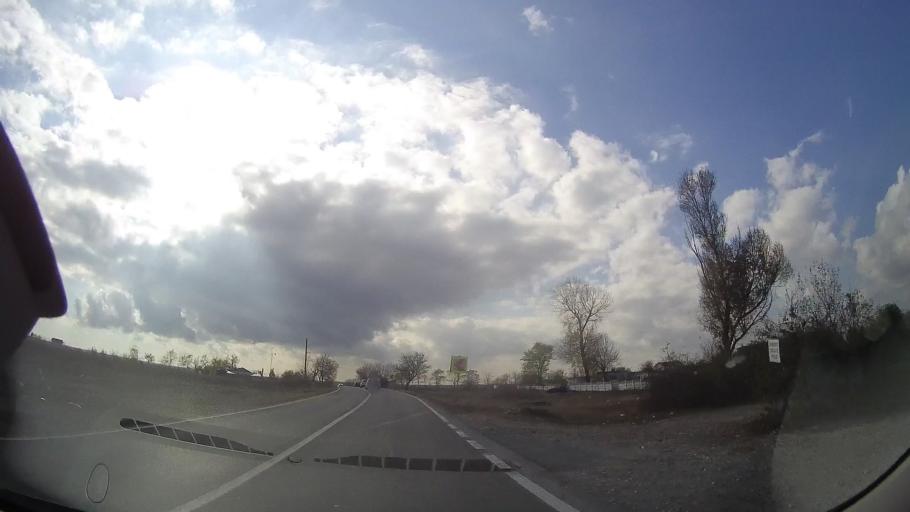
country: RO
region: Constanta
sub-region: Comuna Agigea
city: Agigea
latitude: 44.0724
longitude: 28.5974
